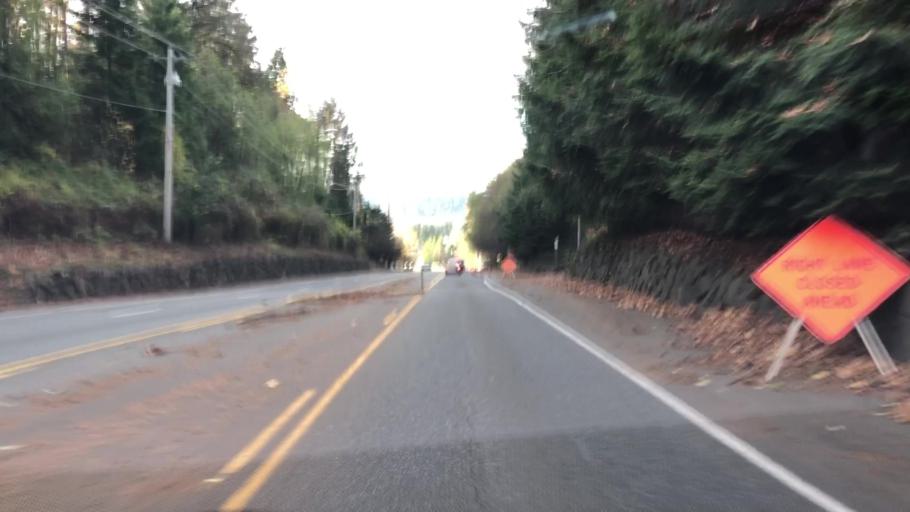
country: US
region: Washington
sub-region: King County
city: Woodinville
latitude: 47.7632
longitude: -122.1396
